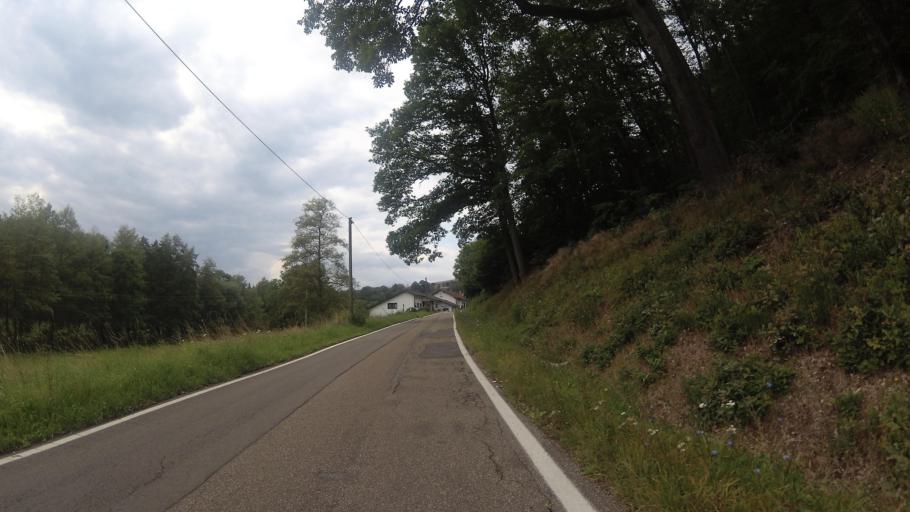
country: DE
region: Rheinland-Pfalz
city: Langenbach
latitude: 49.4926
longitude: 7.3373
